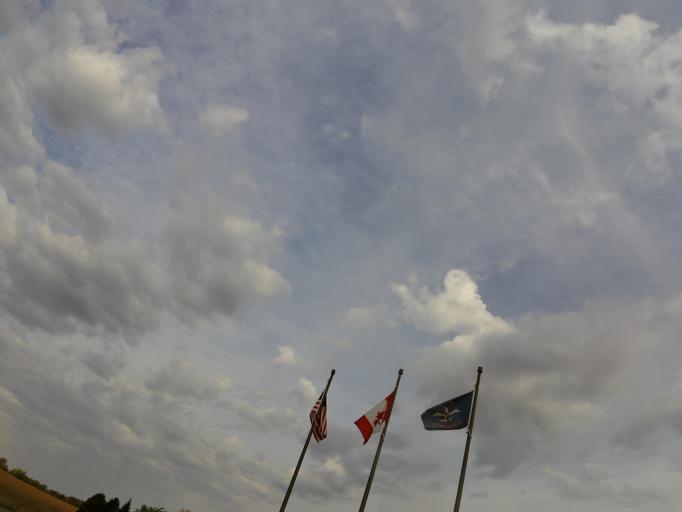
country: US
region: North Dakota
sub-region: Pembina County
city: Cavalier
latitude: 48.7728
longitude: -97.7392
